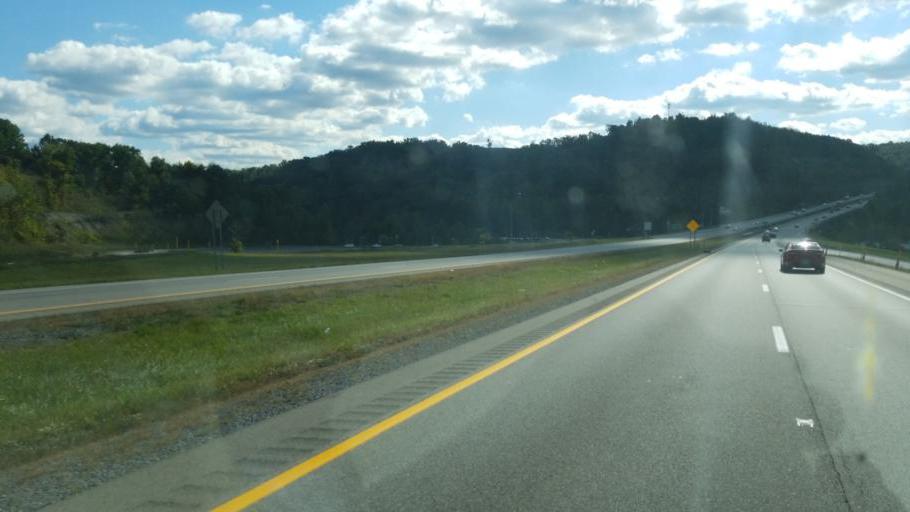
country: US
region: West Virginia
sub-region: Monongalia County
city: Brookhaven
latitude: 39.6145
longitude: -79.9193
